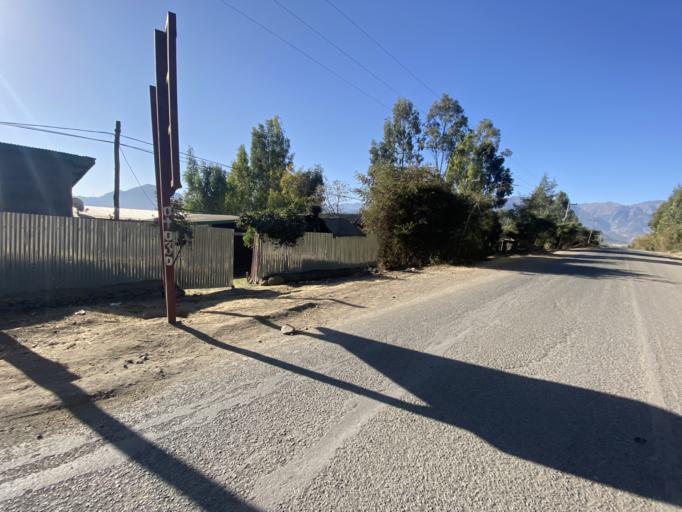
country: ET
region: Amhara
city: Robit
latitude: 11.8268
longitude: 39.5671
